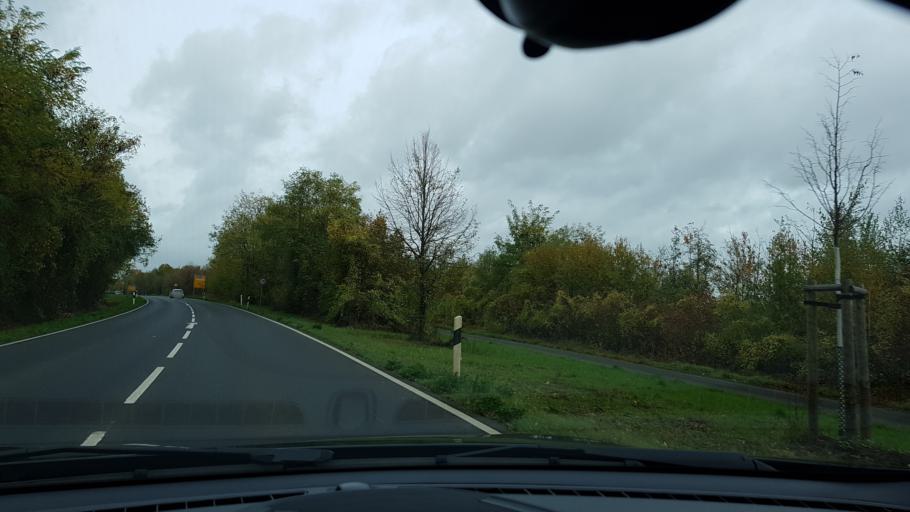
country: DE
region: North Rhine-Westphalia
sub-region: Regierungsbezirk Koln
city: Bedburg
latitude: 51.0025
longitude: 6.5844
